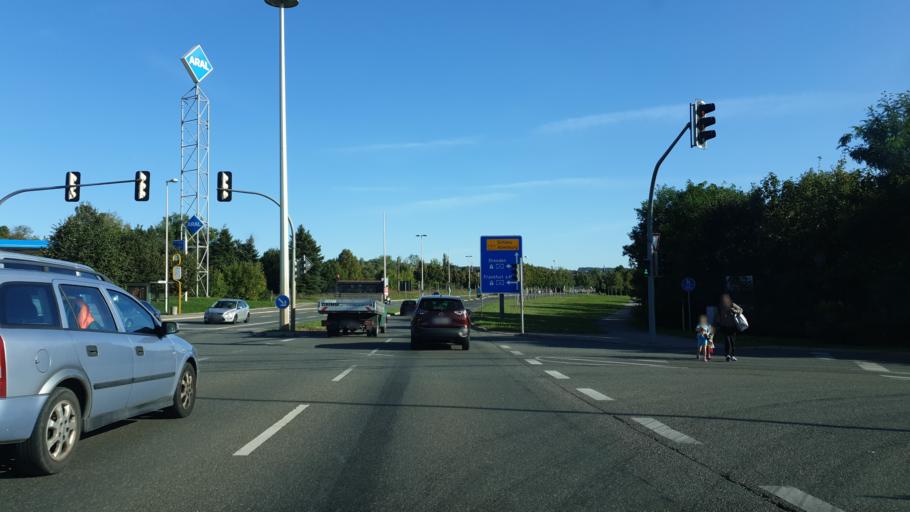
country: DE
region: Thuringia
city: Gera
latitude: 50.9123
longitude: 12.0637
